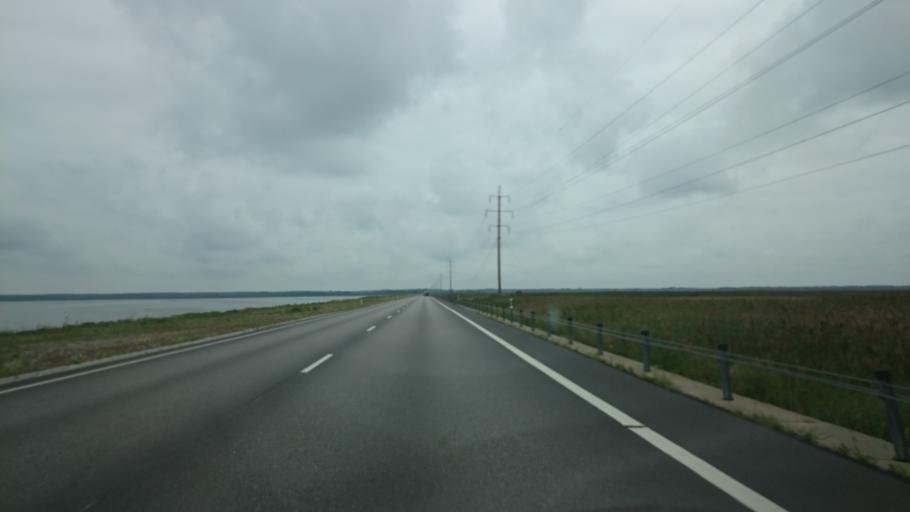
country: EE
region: Saare
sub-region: Orissaare vald
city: Orissaare
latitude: 58.5540
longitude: 23.1440
